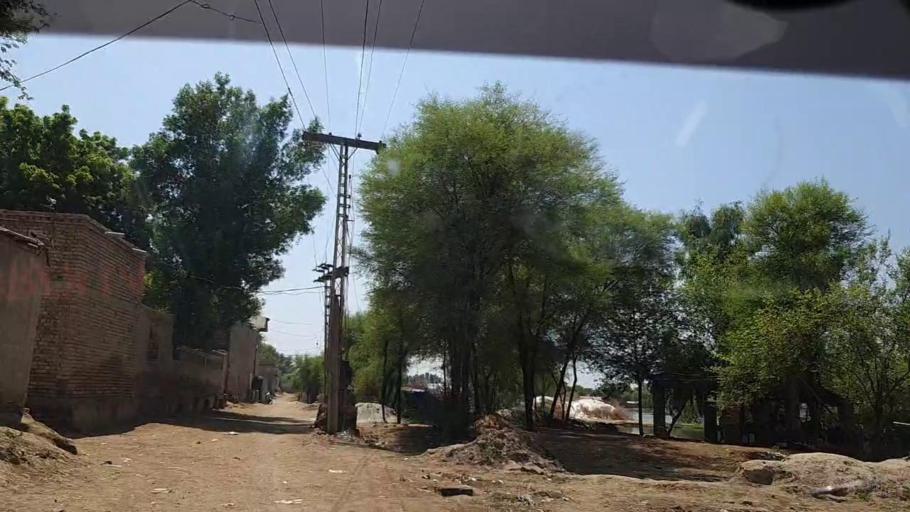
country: PK
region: Sindh
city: Ghauspur
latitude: 28.1606
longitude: 69.1242
